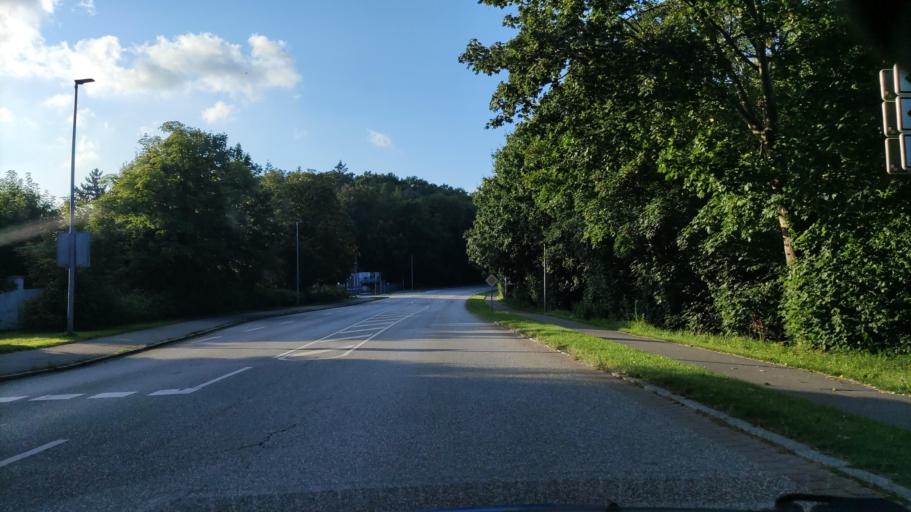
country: DE
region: Schleswig-Holstein
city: Bosdorf
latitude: 54.1496
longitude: 10.4524
